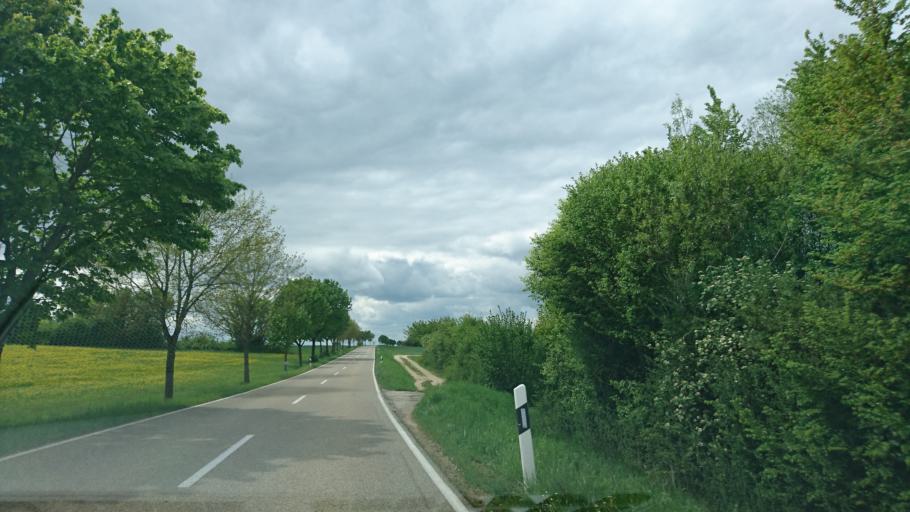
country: DE
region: Bavaria
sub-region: Regierungsbezirk Mittelfranken
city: Langenaltheim
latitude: 48.8928
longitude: 10.9142
